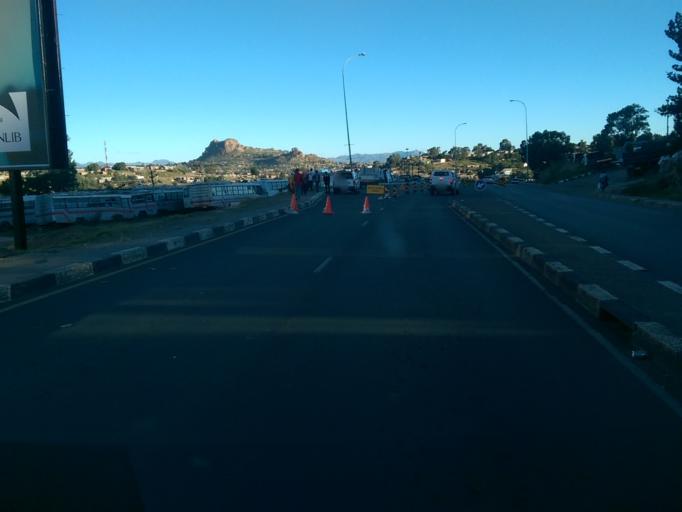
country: LS
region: Maseru
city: Maseru
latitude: -29.3276
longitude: 27.5035
